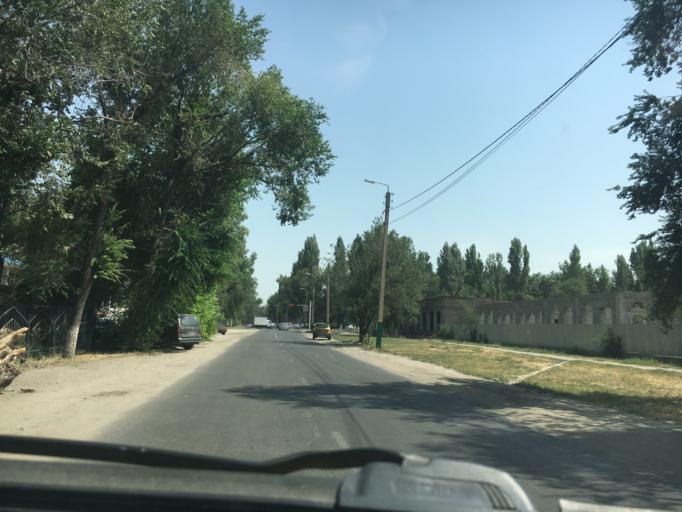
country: KZ
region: Zhambyl
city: Taraz
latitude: 42.8891
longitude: 71.3435
